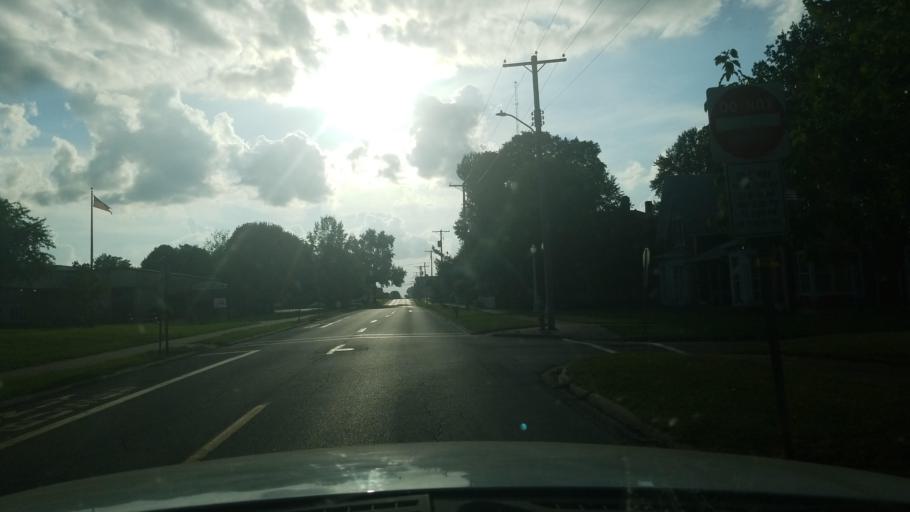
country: US
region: Illinois
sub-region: Saline County
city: Harrisburg
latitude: 37.7342
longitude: -88.5351
